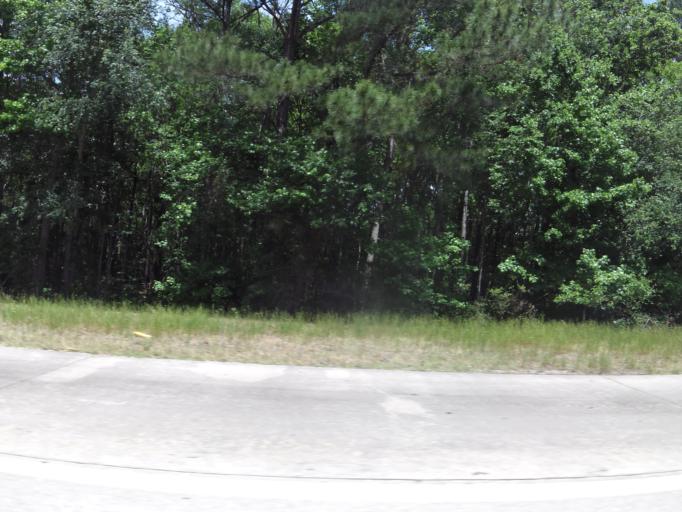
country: US
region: Georgia
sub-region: Bulloch County
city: Brooklet
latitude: 32.2848
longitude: -81.7870
